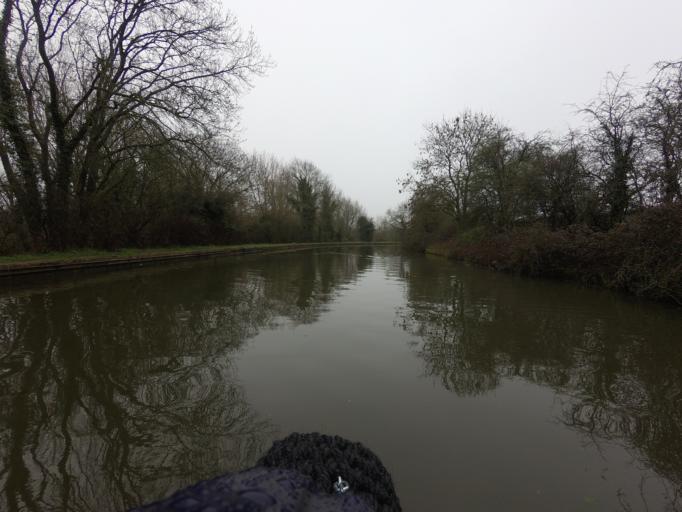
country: GB
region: England
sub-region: Milton Keynes
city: Simpson
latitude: 52.0083
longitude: -0.7163
